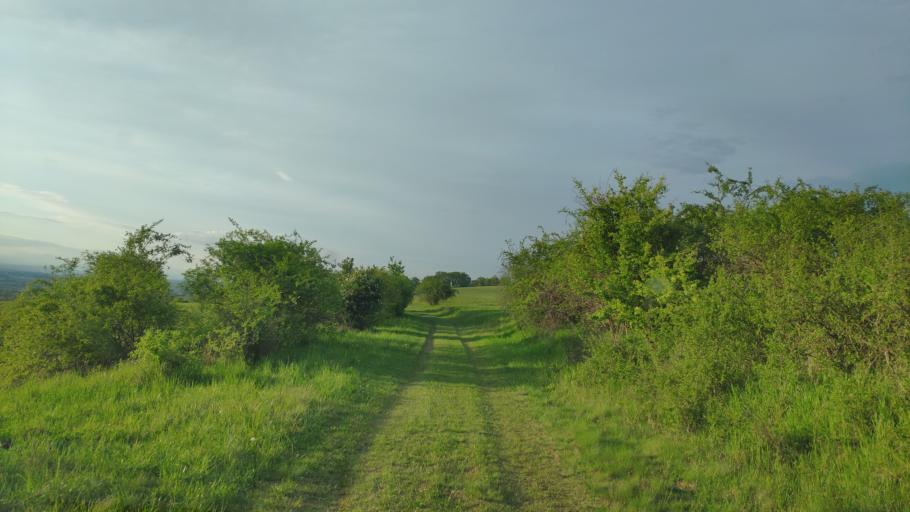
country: SK
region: Kosicky
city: Kosice
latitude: 48.7187
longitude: 21.3553
